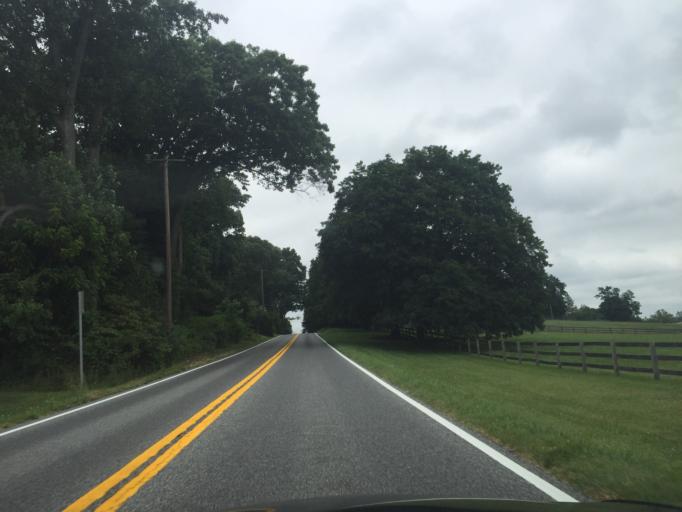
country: US
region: Maryland
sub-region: Harford County
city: Jarrettsville
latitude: 39.5632
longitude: -76.5235
